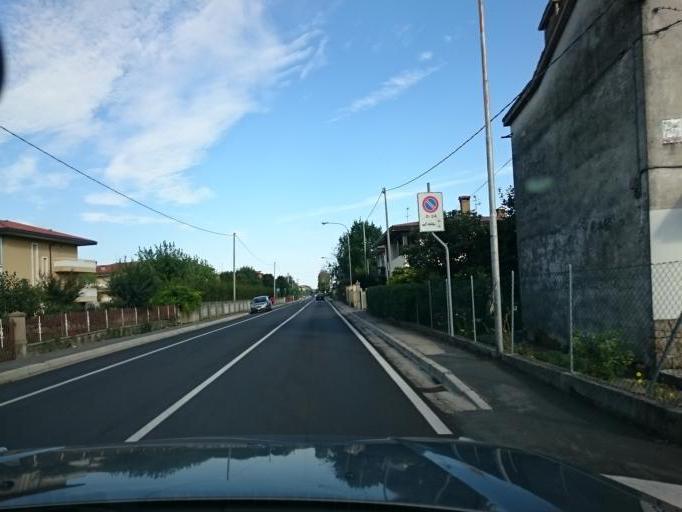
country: IT
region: Veneto
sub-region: Provincia di Padova
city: Torreglia
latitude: 45.3356
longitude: 11.7368
